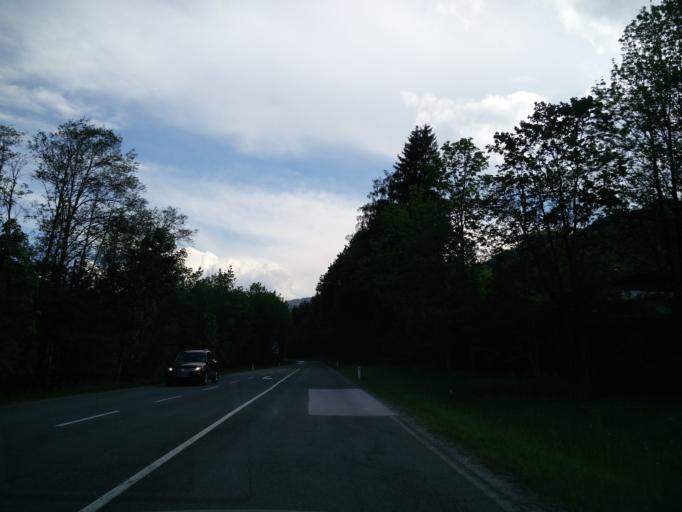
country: AT
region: Tyrol
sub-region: Politischer Bezirk Kitzbuhel
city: Kirchdorf in Tirol
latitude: 47.6030
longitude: 12.4673
